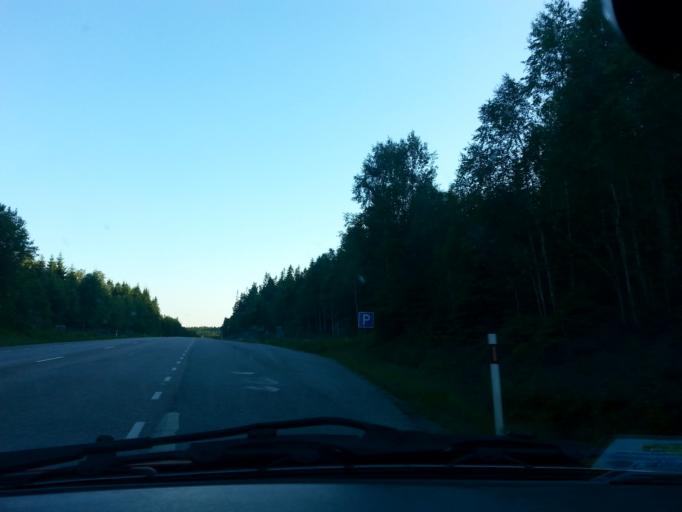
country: SE
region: Vaestra Goetaland
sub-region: Boras Kommun
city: Boras
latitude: 57.6796
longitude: 12.9323
